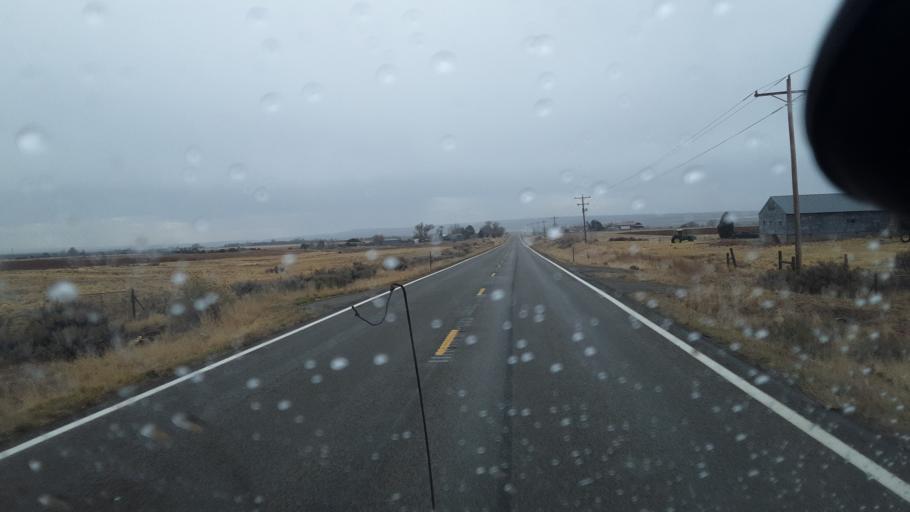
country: US
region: Colorado
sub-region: Montezuma County
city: Mancos
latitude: 37.1173
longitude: -108.1484
